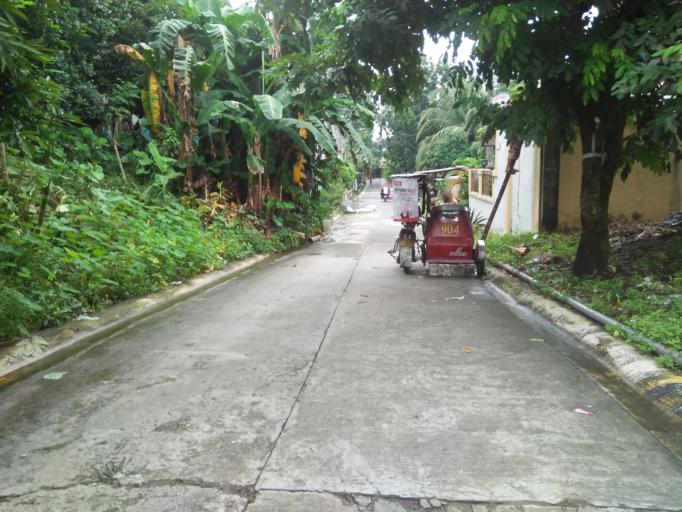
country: PH
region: Central Luzon
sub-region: Province of Bulacan
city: San Jose del Monte
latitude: 14.7485
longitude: 121.0638
